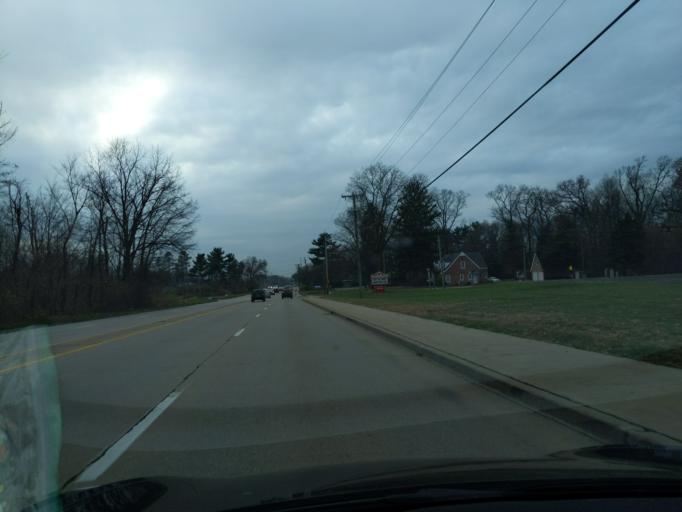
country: US
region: Indiana
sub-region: Saint Joseph County
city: Georgetown
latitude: 41.7232
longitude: -86.2445
